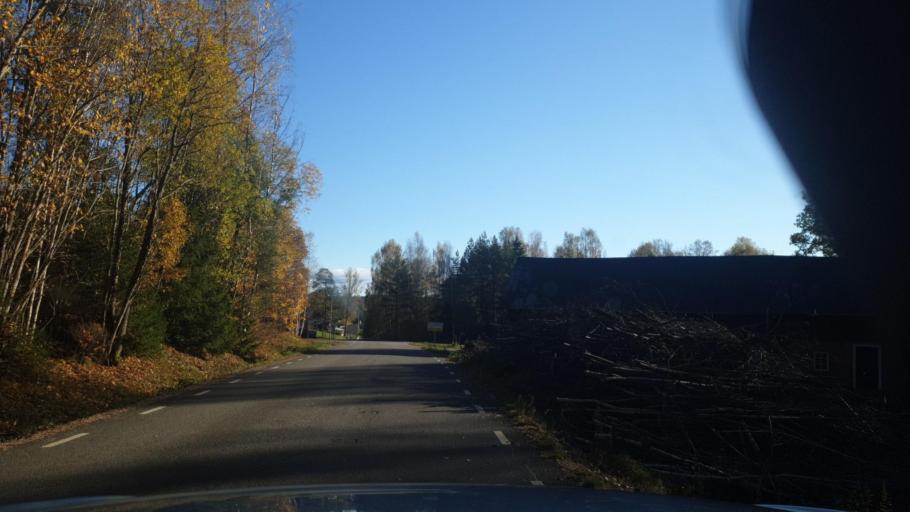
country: SE
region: Vaermland
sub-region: Arvika Kommun
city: Arvika
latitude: 59.6363
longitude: 12.8172
